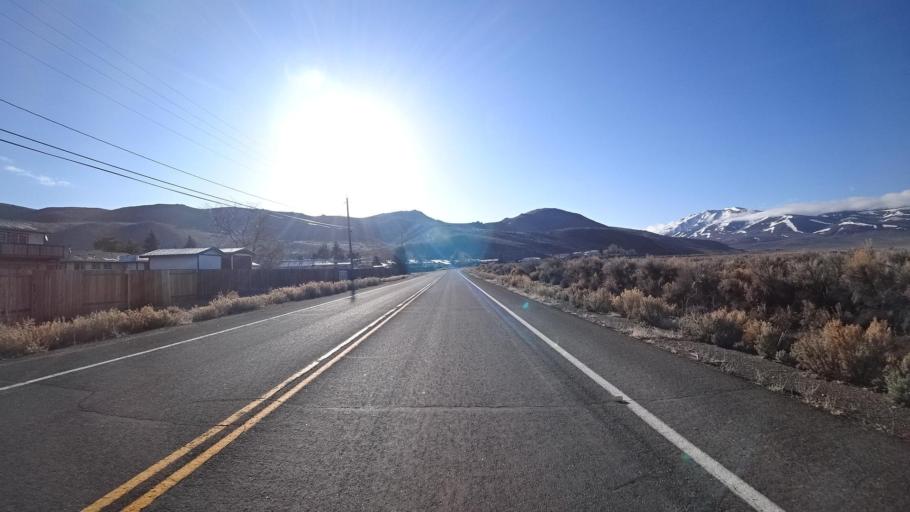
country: US
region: Nevada
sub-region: Washoe County
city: Cold Springs
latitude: 39.6702
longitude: -119.9636
